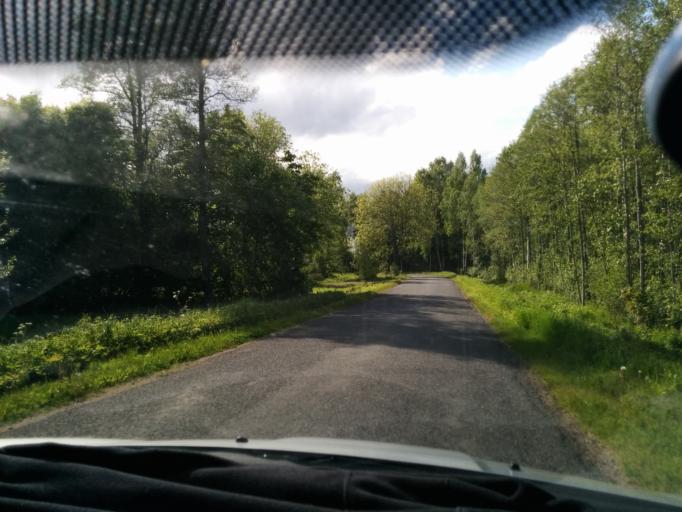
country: EE
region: Harju
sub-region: Loksa linn
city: Loksa
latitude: 59.6144
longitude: 25.6967
